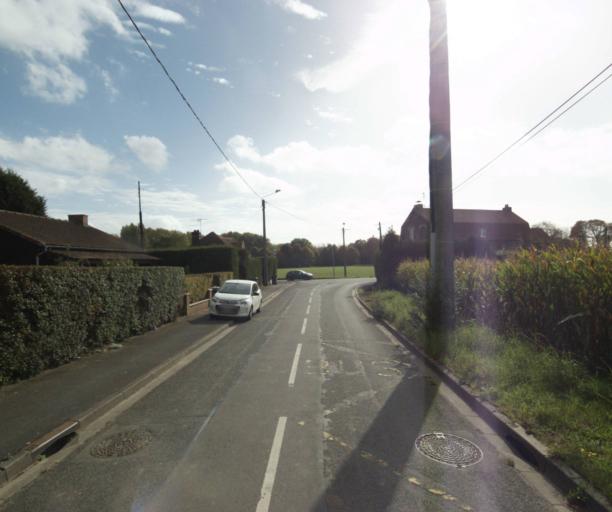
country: FR
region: Nord-Pas-de-Calais
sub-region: Departement du Nord
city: Salome
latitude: 50.5315
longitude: 2.8272
